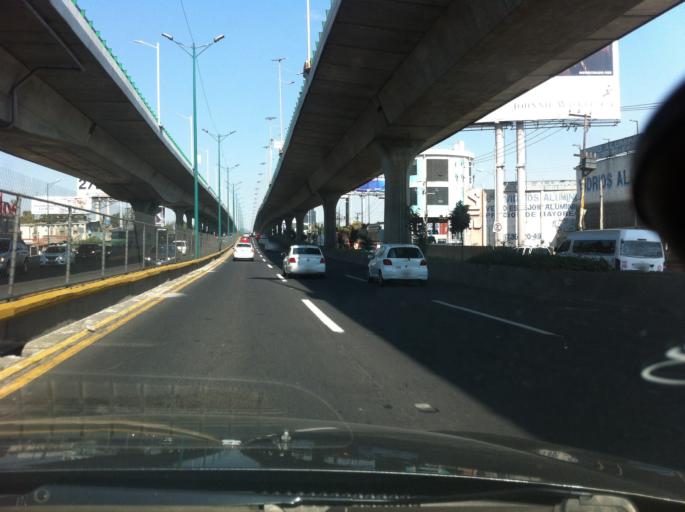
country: MX
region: Mexico
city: Naucalpan de Juarez
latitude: 19.4713
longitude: -99.2276
